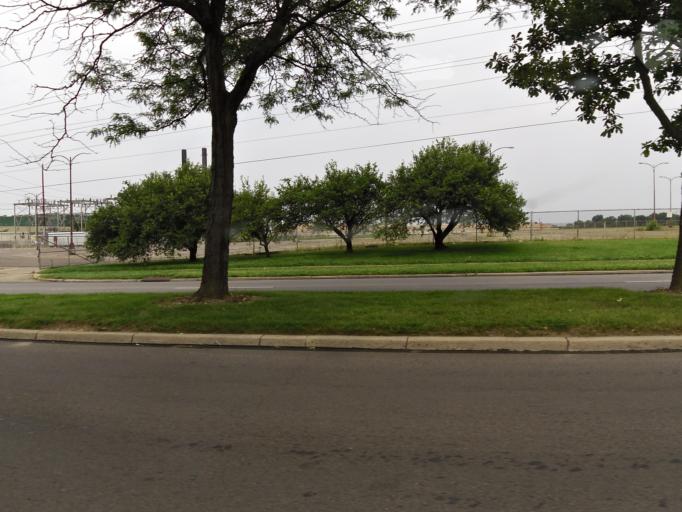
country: US
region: Ohio
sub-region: Montgomery County
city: Kettering
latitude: 39.7120
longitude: -84.1238
